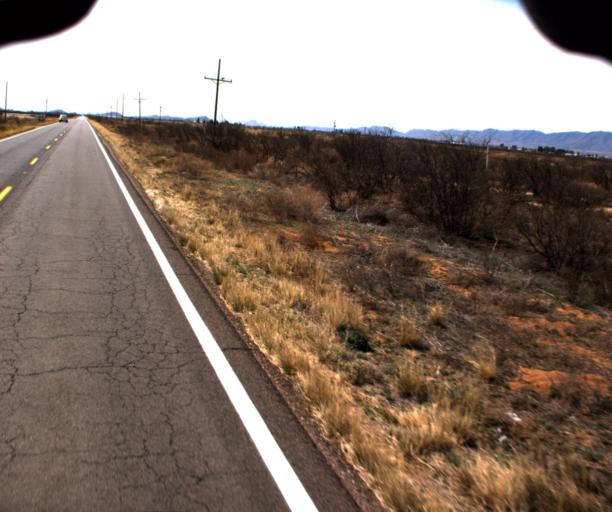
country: US
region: Arizona
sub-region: Cochise County
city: Willcox
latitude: 32.0003
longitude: -109.8611
